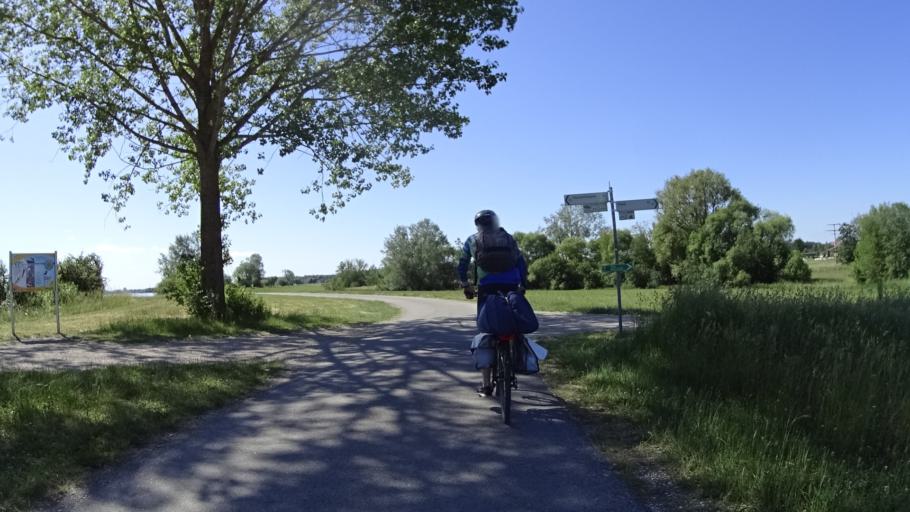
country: DE
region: Bavaria
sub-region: Regierungsbezirk Mittelfranken
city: Muhr am See
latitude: 49.1322
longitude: 10.7146
